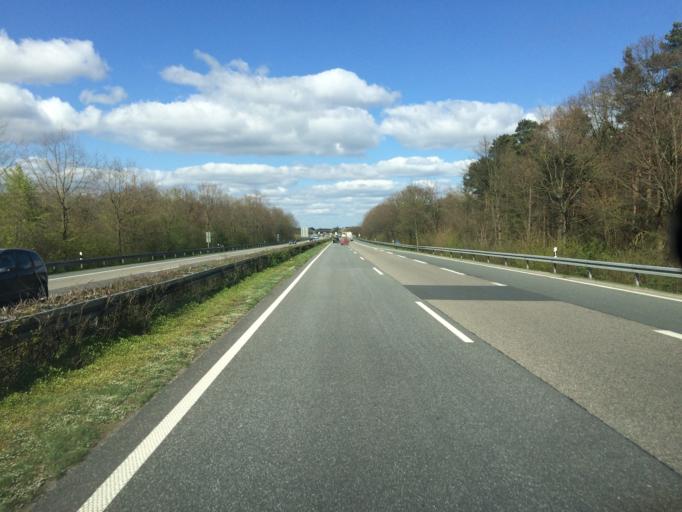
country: DE
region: North Rhine-Westphalia
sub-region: Regierungsbezirk Munster
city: Heek
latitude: 52.1235
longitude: 7.0874
